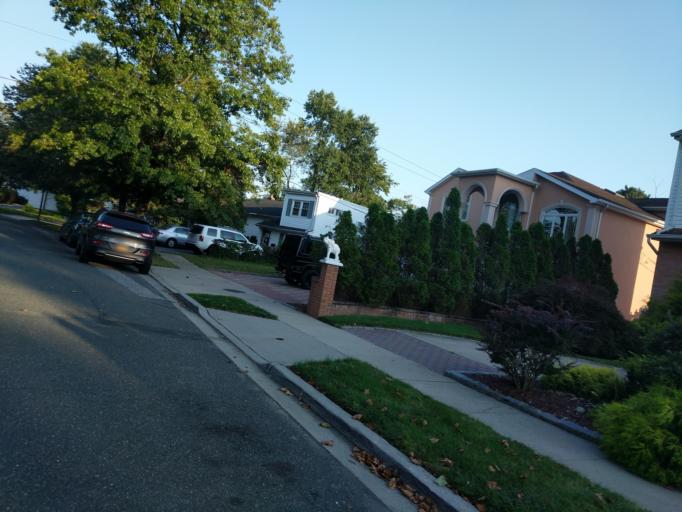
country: US
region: New York
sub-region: Nassau County
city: South Valley Stream
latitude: 40.6557
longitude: -73.7172
